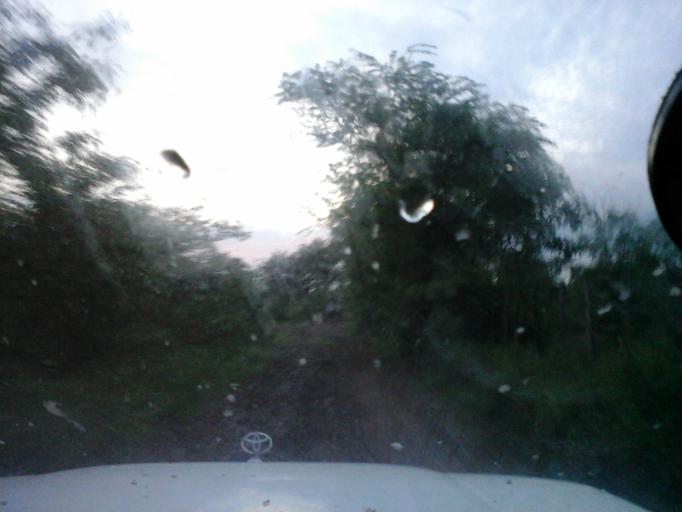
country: CO
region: Cesar
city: Agustin Codazzi
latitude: 10.1592
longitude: -73.2054
